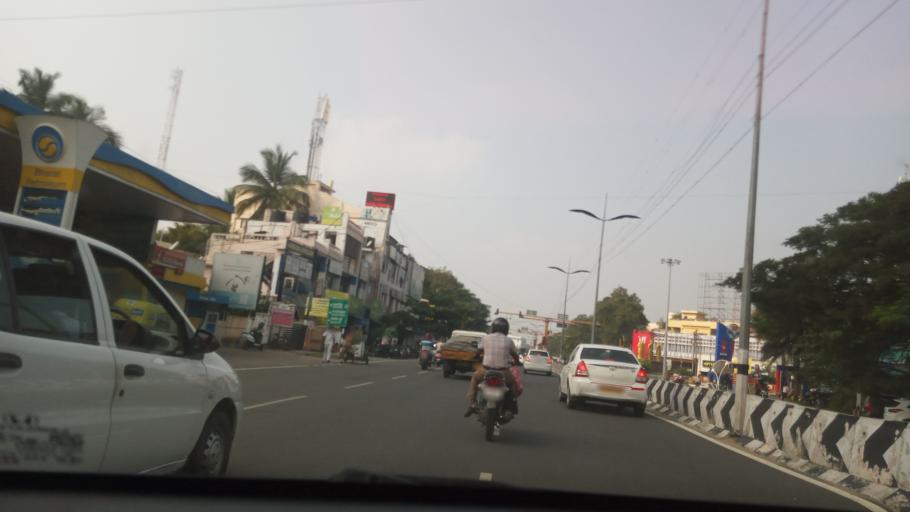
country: IN
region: Tamil Nadu
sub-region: Coimbatore
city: Coimbatore
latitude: 11.0058
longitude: 76.9756
